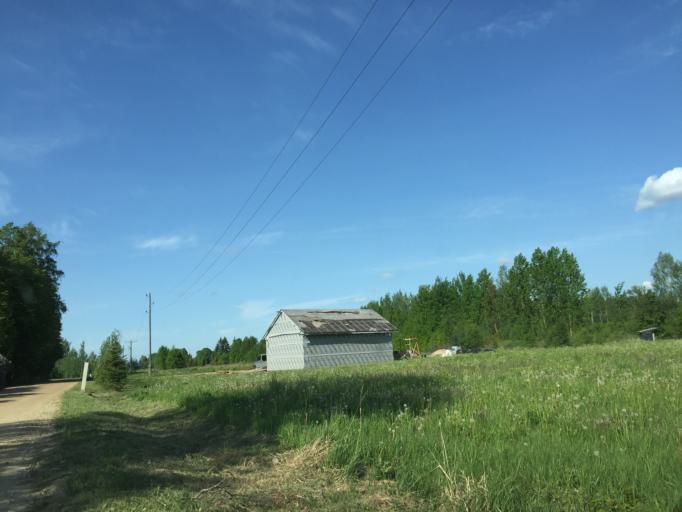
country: LV
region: Salaspils
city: Salaspils
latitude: 56.8224
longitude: 24.3645
